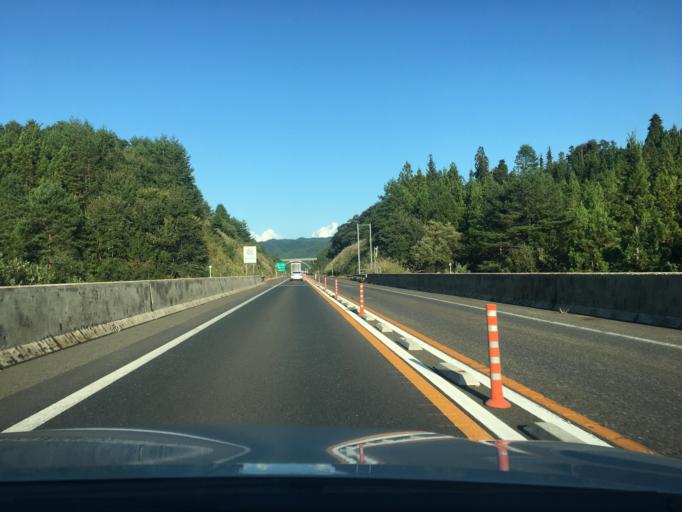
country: JP
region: Fukushima
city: Kitakata
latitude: 37.5648
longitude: 139.6206
